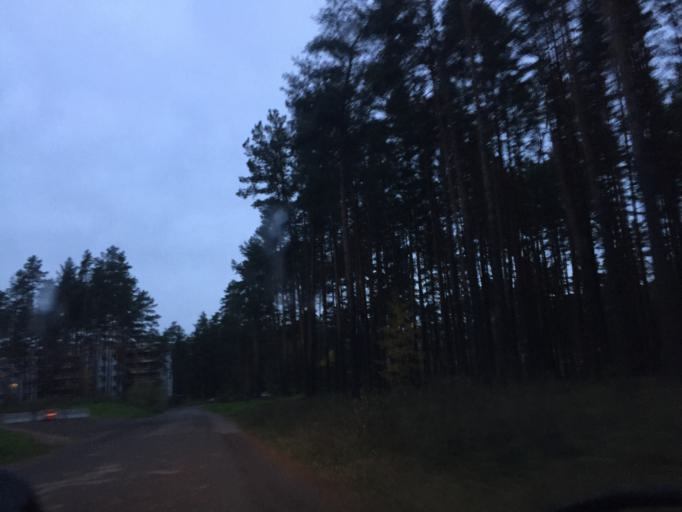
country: LV
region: Adazi
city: Adazi
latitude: 57.0894
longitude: 24.3630
